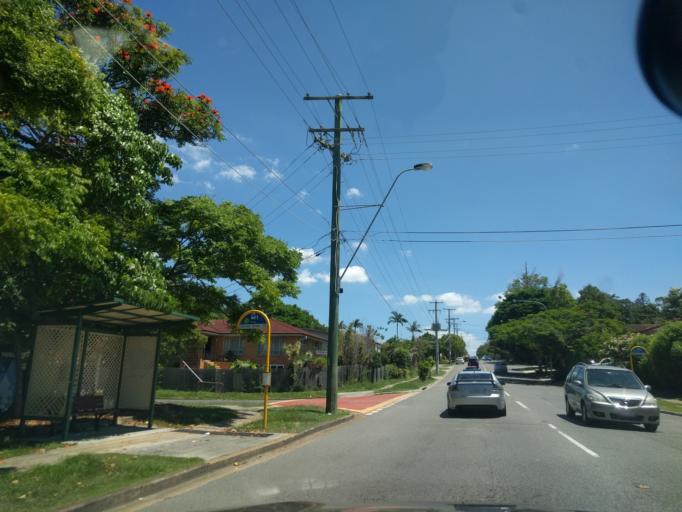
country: AU
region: Queensland
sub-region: Brisbane
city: Chermside West
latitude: -27.3654
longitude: 153.0161
